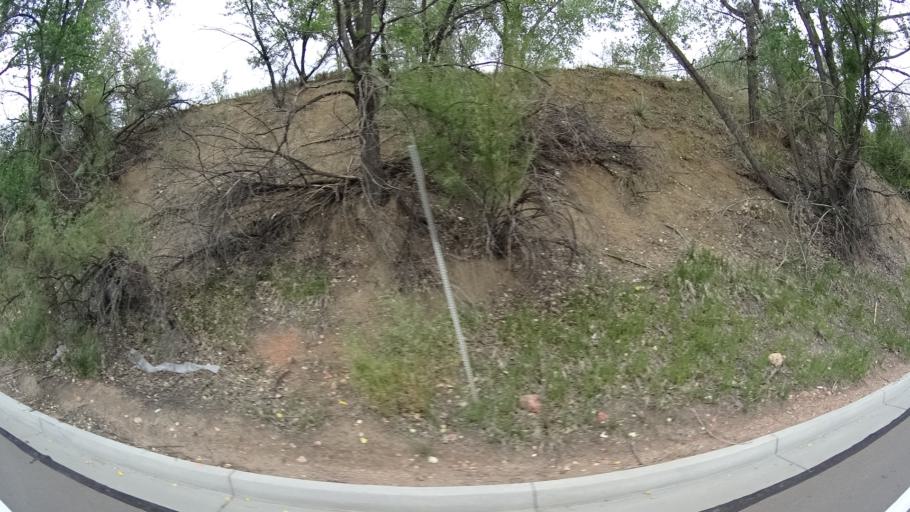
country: US
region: Colorado
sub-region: El Paso County
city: Colorado Springs
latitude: 38.8764
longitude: -104.8421
